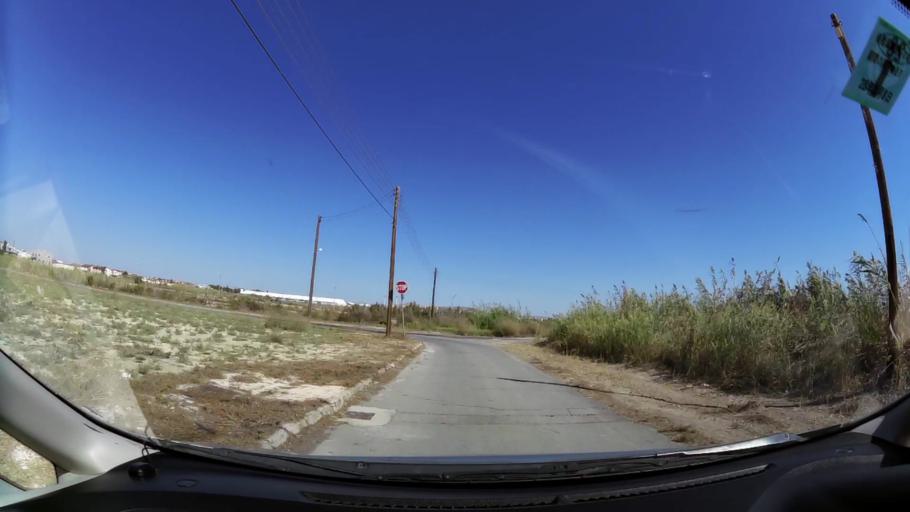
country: CY
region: Larnaka
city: Livadia
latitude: 34.9379
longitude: 33.6335
